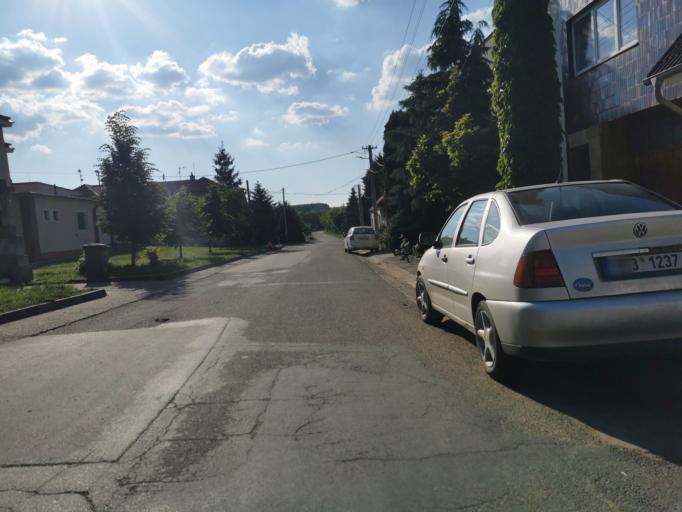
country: CZ
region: South Moravian
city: Knezdub
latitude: 48.8794
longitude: 17.3559
